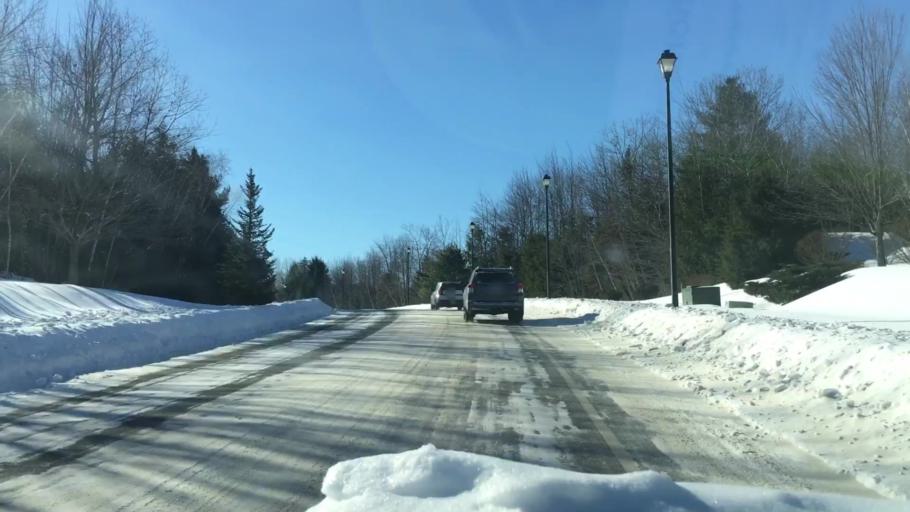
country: US
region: Maine
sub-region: Sagadahoc County
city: Topsham
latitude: 43.9392
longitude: -69.9557
